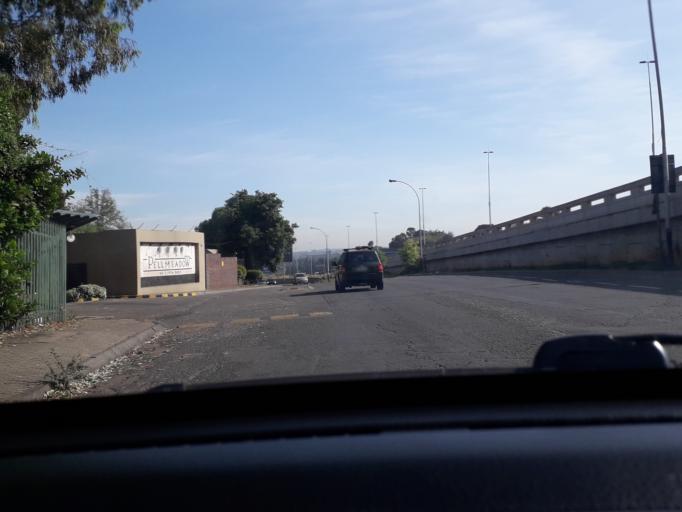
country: ZA
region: Gauteng
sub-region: Ekurhuleni Metropolitan Municipality
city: Germiston
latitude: -26.1650
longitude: 28.1328
